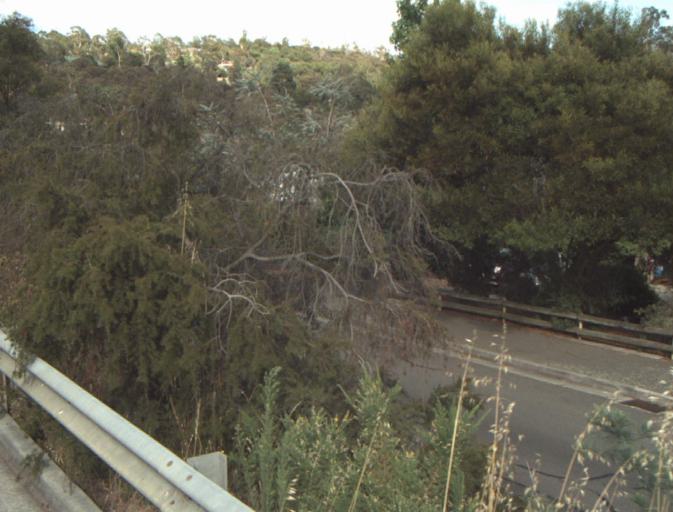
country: AU
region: Tasmania
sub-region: Launceston
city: Summerhill
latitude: -41.4612
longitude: 147.1262
